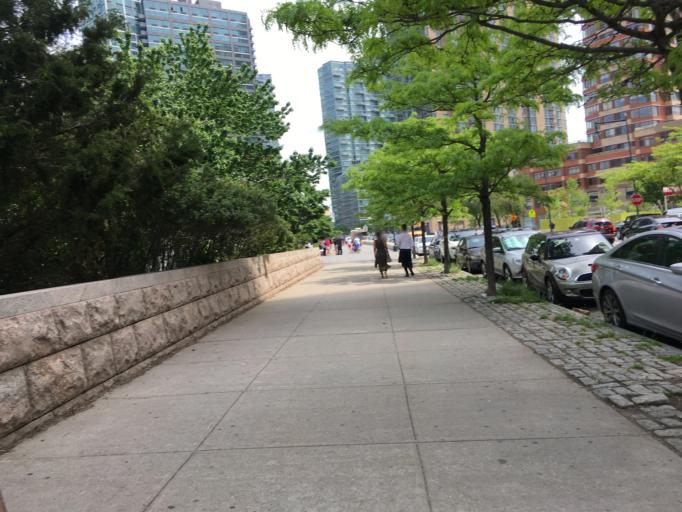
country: US
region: New York
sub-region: Queens County
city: Long Island City
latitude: 40.7441
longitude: -73.9590
